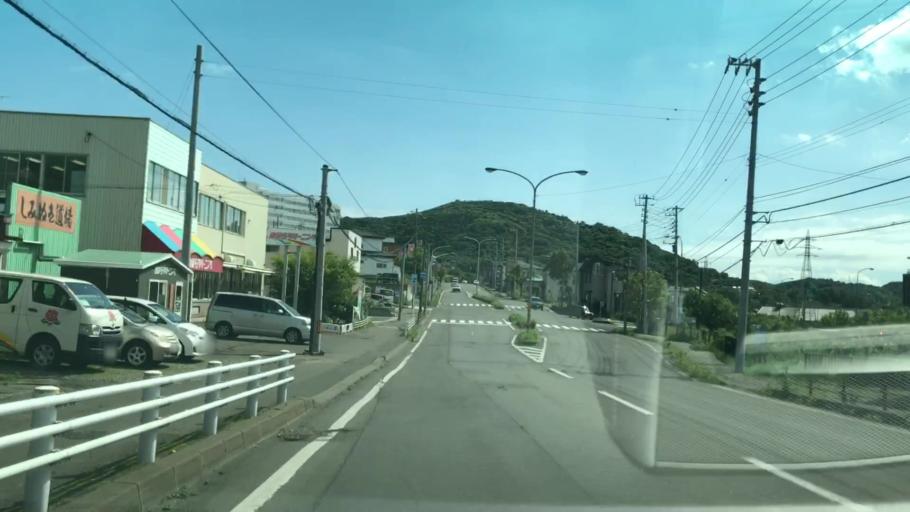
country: JP
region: Hokkaido
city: Muroran
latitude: 42.3249
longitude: 140.9965
